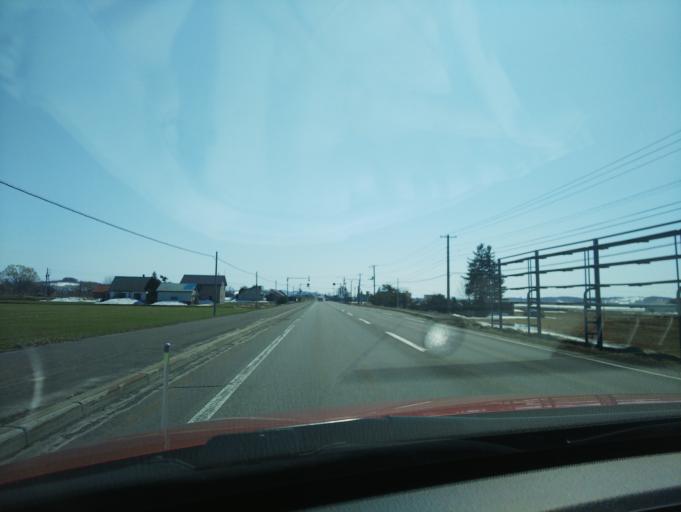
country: JP
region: Hokkaido
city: Nayoro
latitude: 44.2022
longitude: 142.3949
